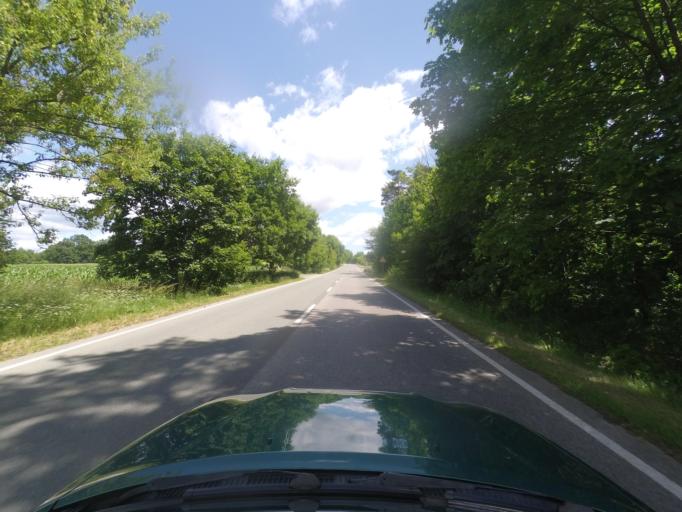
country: CZ
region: Kralovehradecky
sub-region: Okres Rychnov nad Kneznou
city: Rychnov nad Kneznou
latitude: 50.1650
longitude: 16.3033
